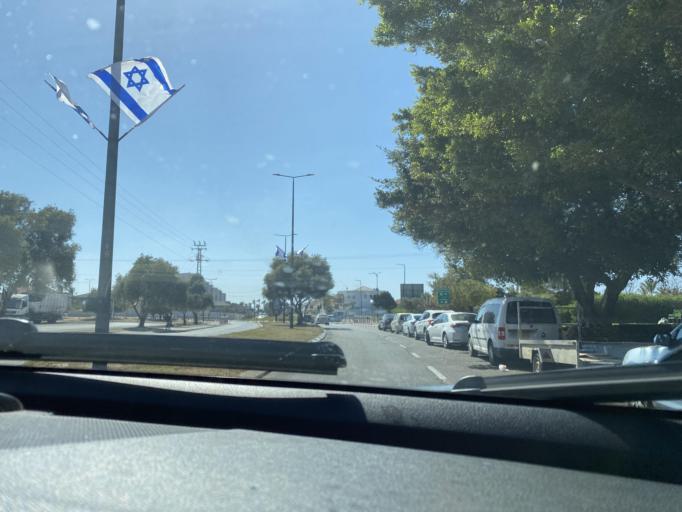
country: IL
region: Southern District
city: Ashqelon
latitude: 31.6840
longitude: 34.5674
